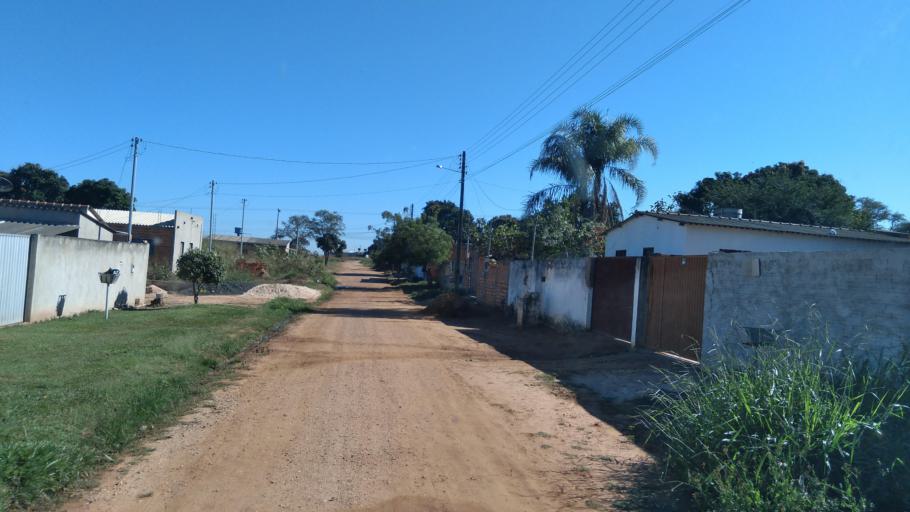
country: BR
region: Goias
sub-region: Mineiros
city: Mineiros
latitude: -17.5917
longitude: -52.5579
